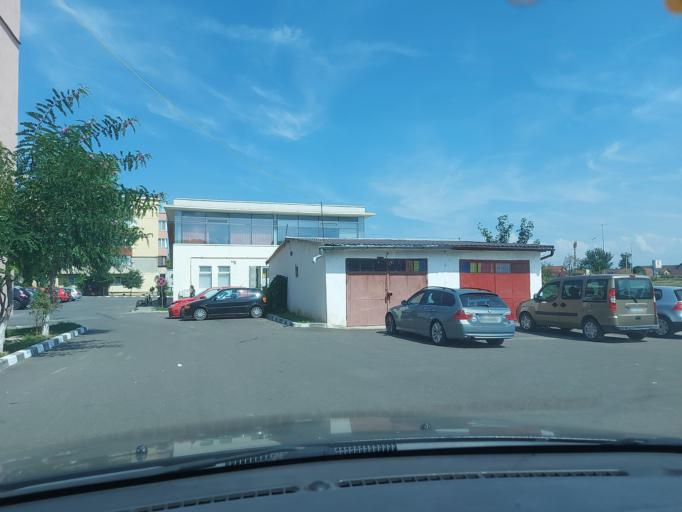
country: RO
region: Brasov
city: Codlea
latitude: 45.6901
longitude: 25.4464
